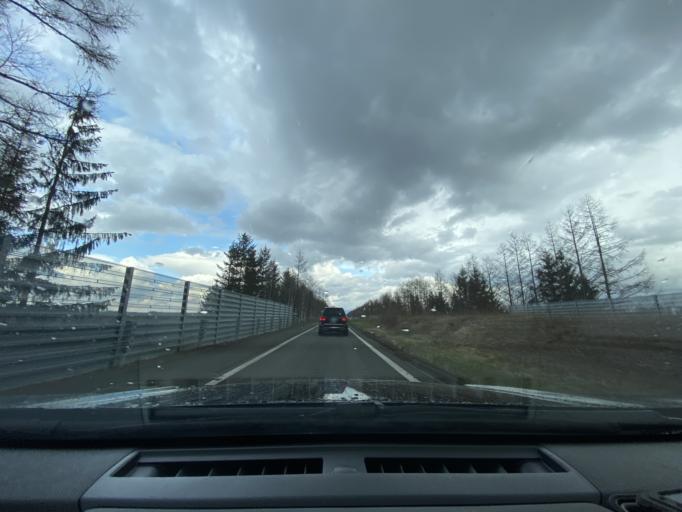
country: JP
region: Hokkaido
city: Otofuke
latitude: 42.9804
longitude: 142.9656
